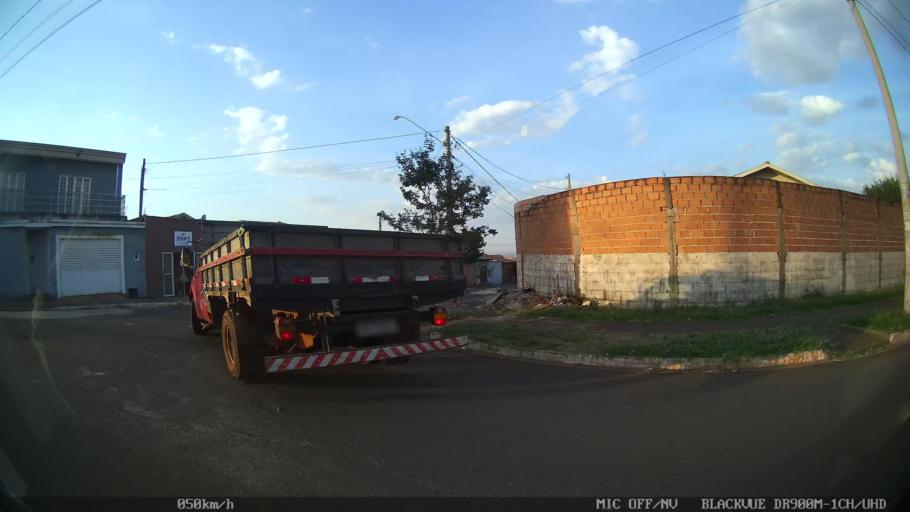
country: BR
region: Sao Paulo
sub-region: Ribeirao Preto
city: Ribeirao Preto
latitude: -21.1481
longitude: -47.8500
